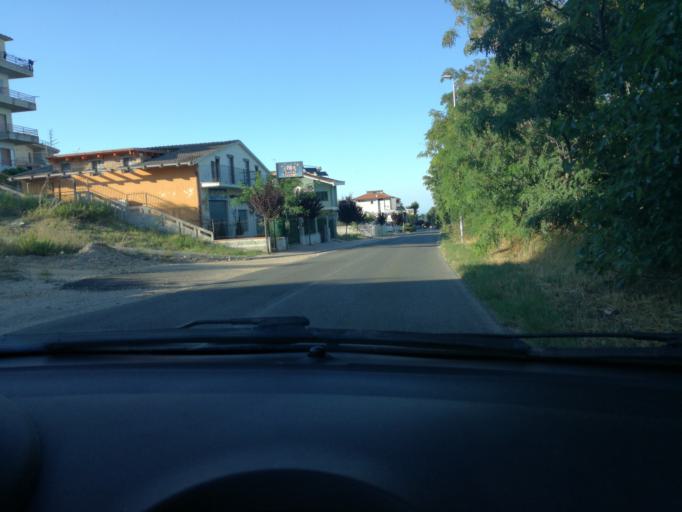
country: IT
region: Molise
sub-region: Provincia di Campobasso
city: Guglionesi
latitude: 41.9209
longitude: 14.9167
